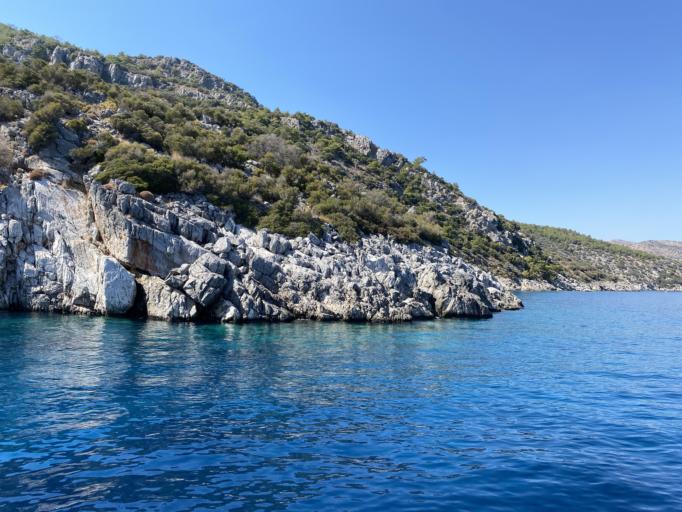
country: TR
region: Mugla
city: Datca
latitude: 36.6743
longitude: 27.6736
